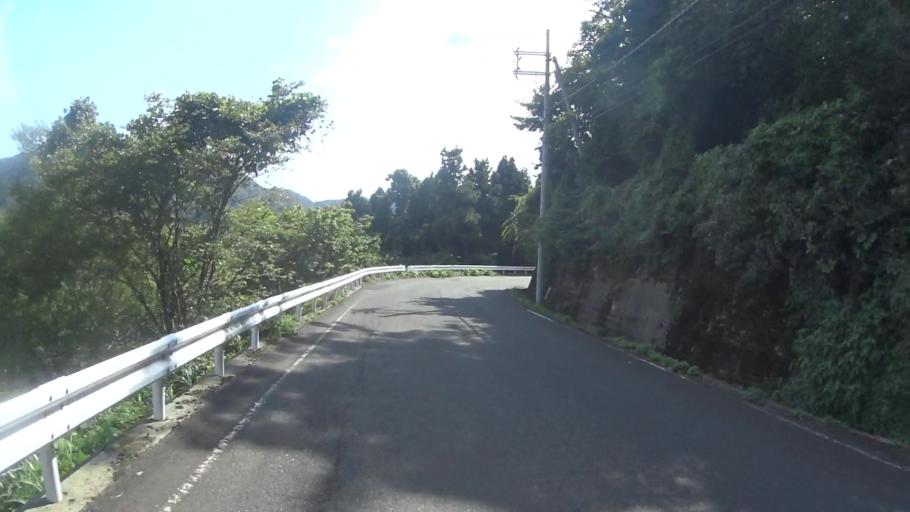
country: JP
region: Kyoto
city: Miyazu
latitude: 35.7107
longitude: 135.1940
